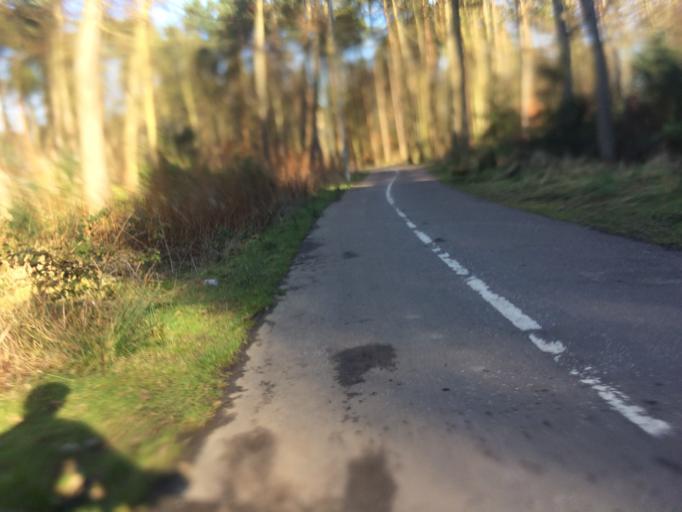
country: GB
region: Scotland
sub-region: Fife
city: Glenrothes
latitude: 56.1895
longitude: -3.1630
